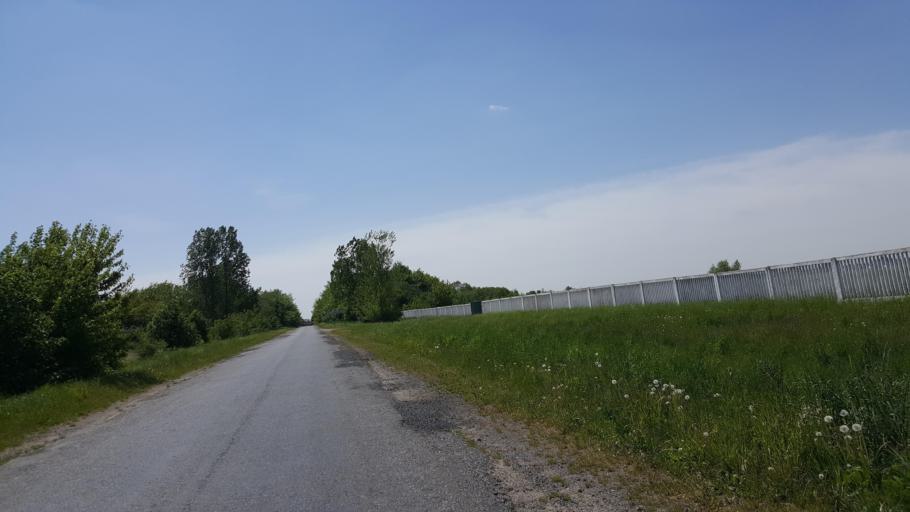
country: BY
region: Brest
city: Charnawchytsy
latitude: 52.2307
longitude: 23.7419
